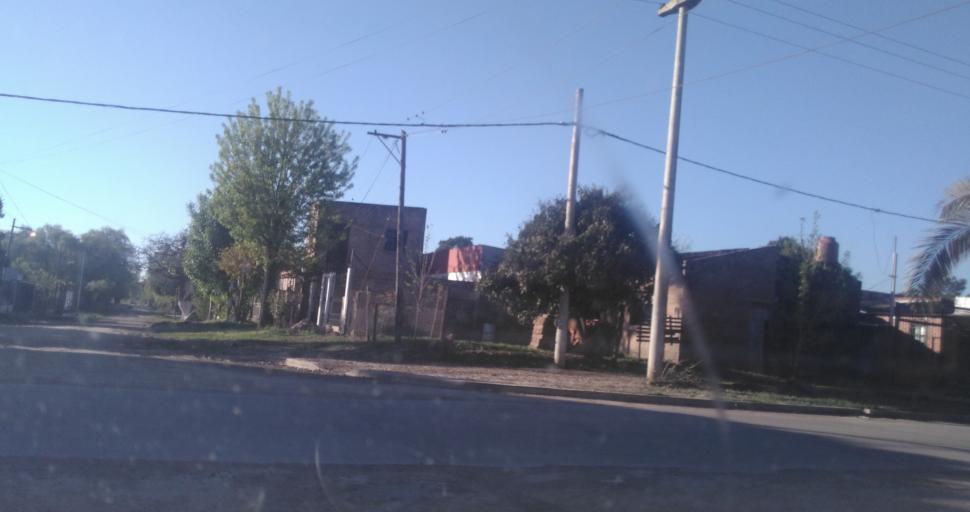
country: AR
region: Chaco
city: Fontana
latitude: -27.4249
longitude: -59.0223
